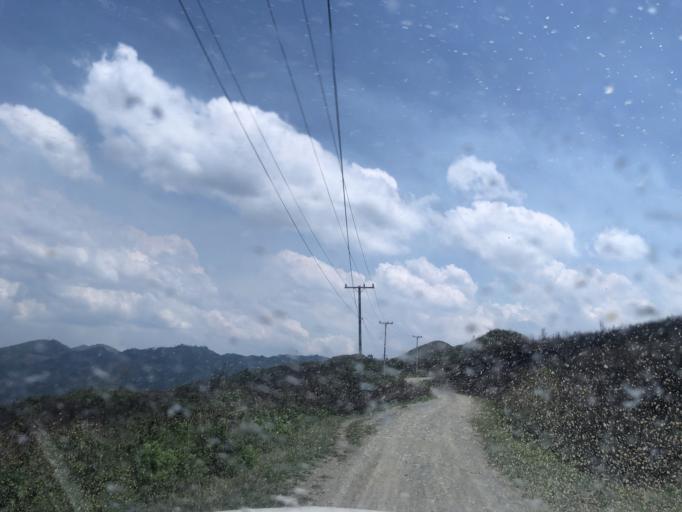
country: LA
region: Phongsali
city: Phongsali
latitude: 21.4173
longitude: 102.1849
